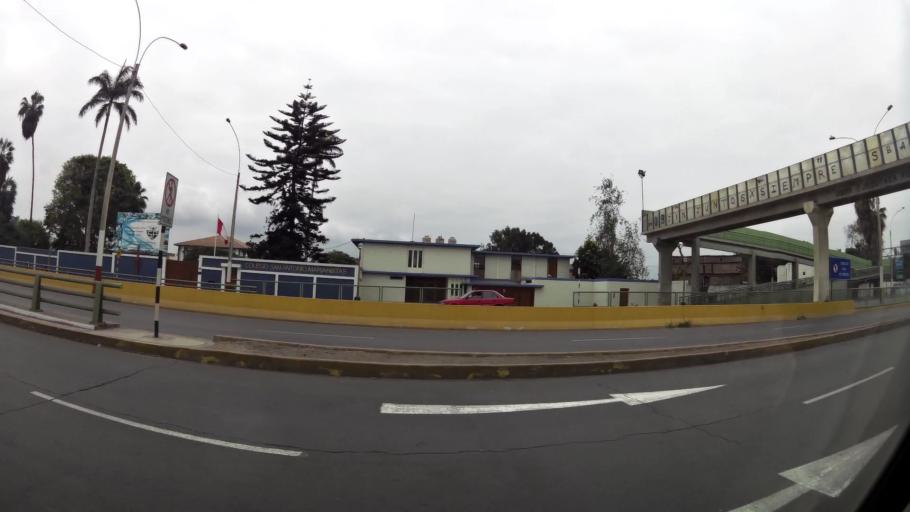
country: PE
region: Callao
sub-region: Callao
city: Callao
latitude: -12.0610
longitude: -77.1255
